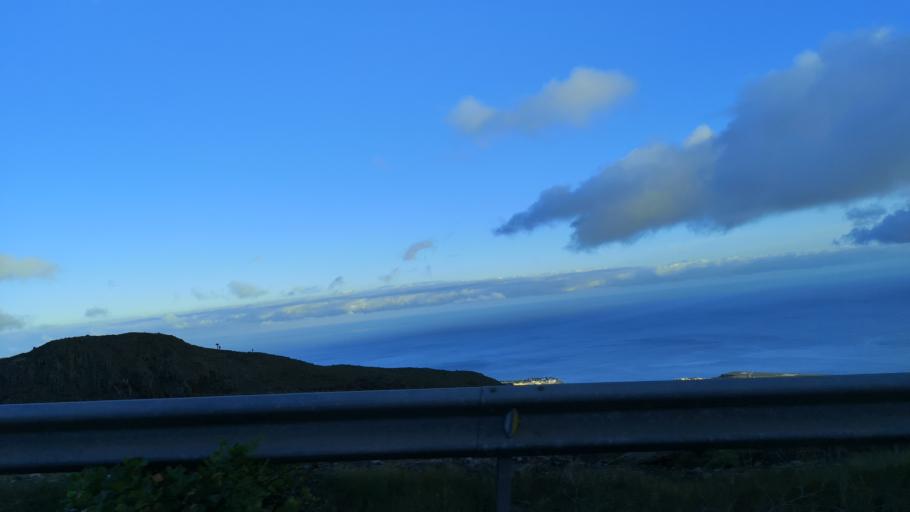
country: ES
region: Canary Islands
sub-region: Provincia de Santa Cruz de Tenerife
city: Alajero
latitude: 28.0522
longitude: -17.2323
